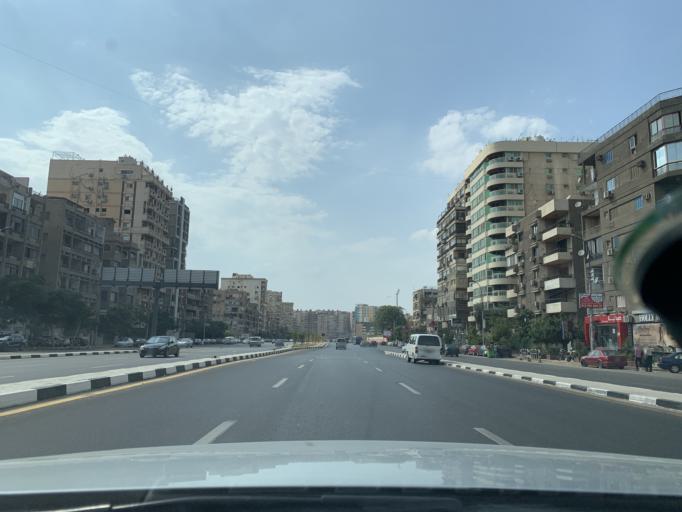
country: EG
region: Muhafazat al Qalyubiyah
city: Al Khankah
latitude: 30.1131
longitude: 31.3446
